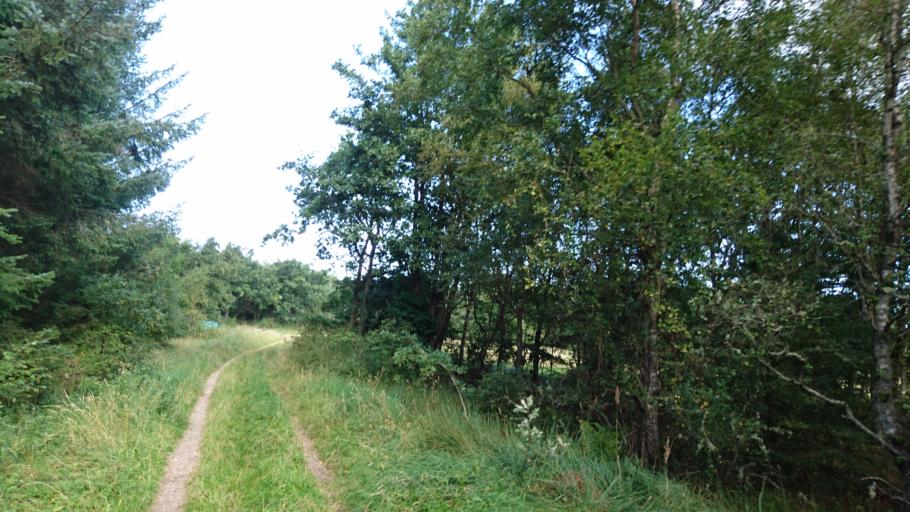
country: DK
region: North Denmark
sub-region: Frederikshavn Kommune
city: Skagen
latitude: 57.7155
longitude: 10.5230
